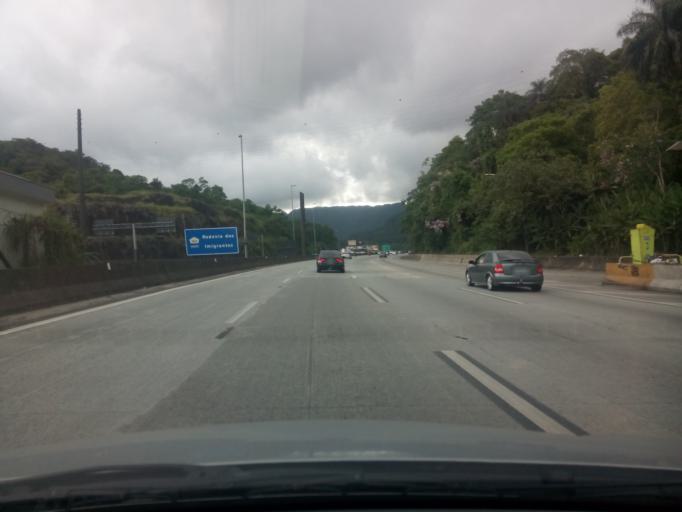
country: BR
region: Sao Paulo
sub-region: Cubatao
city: Cubatao
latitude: -23.9024
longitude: -46.4611
